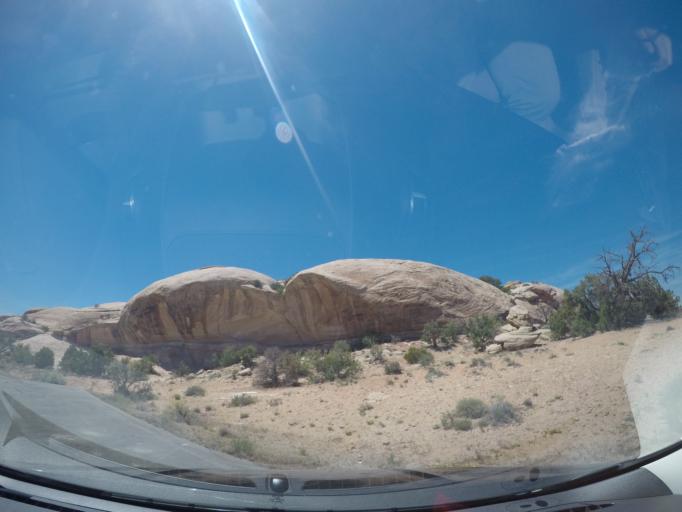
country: US
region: Utah
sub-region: Grand County
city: Moab
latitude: 38.6456
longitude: -109.7364
